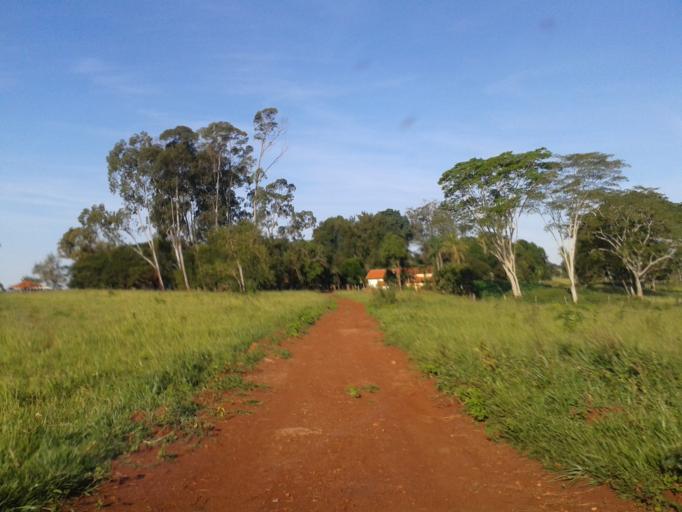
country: BR
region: Minas Gerais
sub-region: Santa Vitoria
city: Santa Vitoria
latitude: -19.0005
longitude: -50.3452
